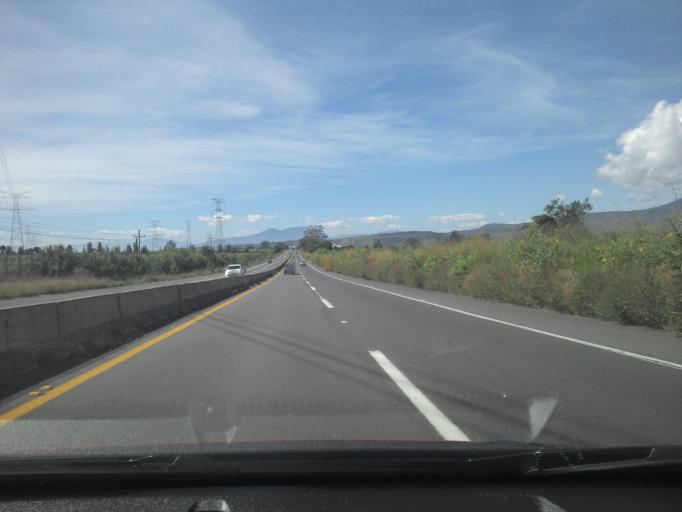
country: MX
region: Jalisco
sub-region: Tala
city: Los Ruisenores
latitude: 20.7117
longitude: -103.6599
